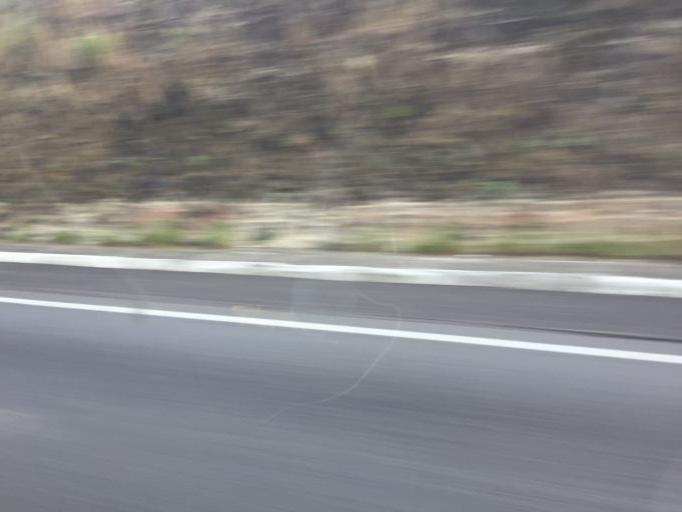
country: MX
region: Michoacan
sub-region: Zinapecuaro
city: Francisco Villa
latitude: 19.8824
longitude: -100.9271
